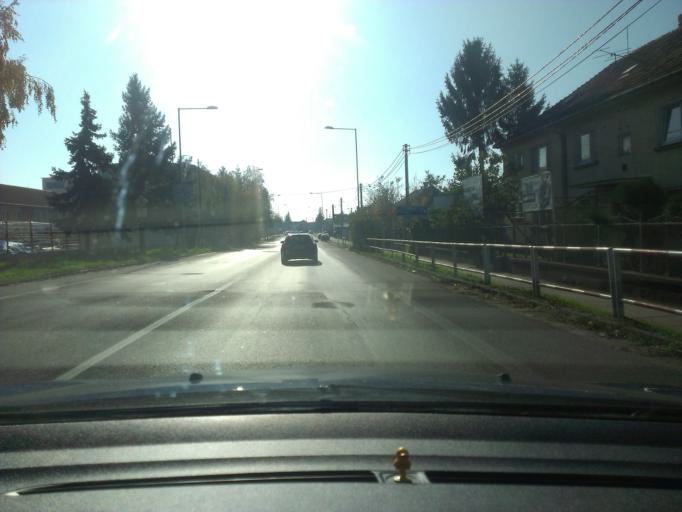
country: SK
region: Nitriansky
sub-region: Okres Nove Zamky
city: Nove Zamky
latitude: 47.9834
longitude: 18.1766
